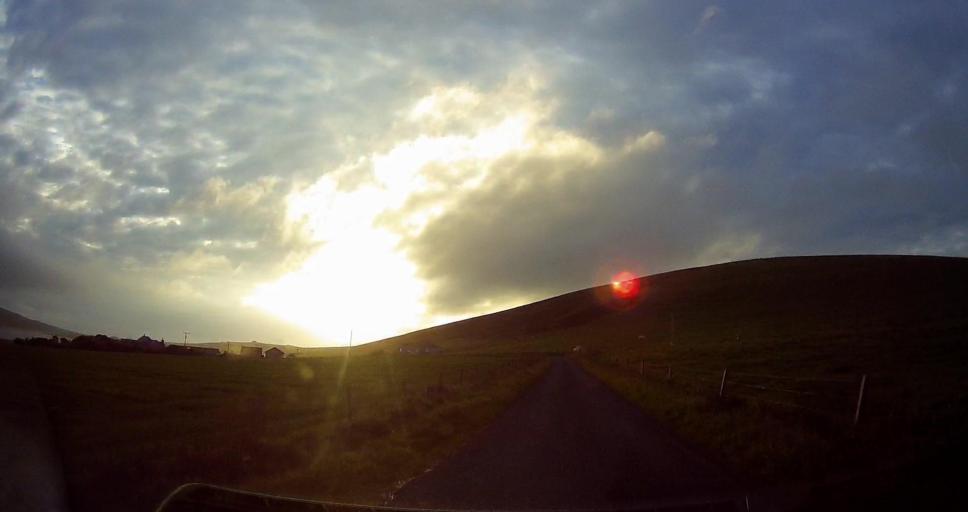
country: GB
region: Scotland
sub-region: Orkney Islands
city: Stromness
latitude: 59.1148
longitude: -3.2544
